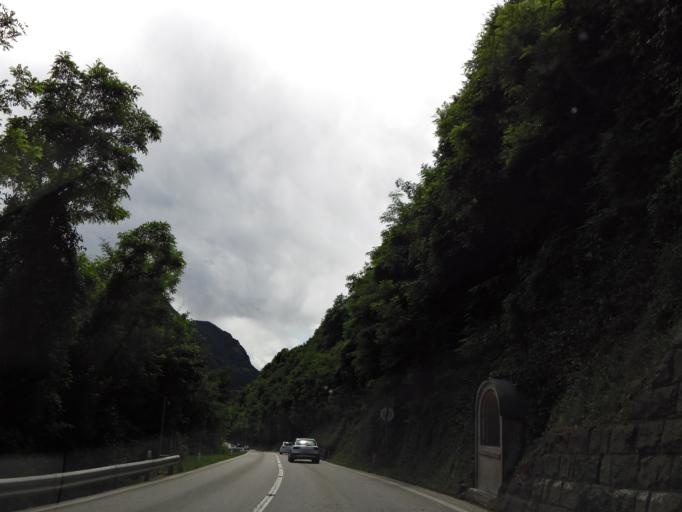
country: IT
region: Trentino-Alto Adige
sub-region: Bolzano
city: Barbiano
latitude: 46.6112
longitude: 11.5332
